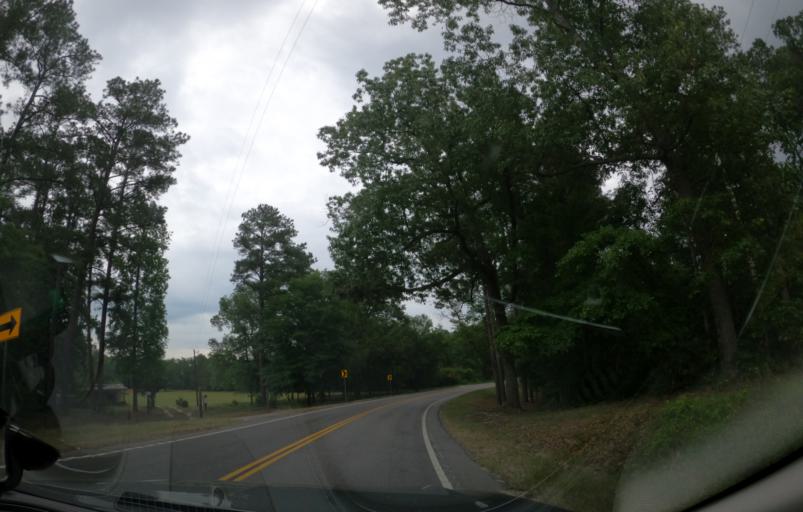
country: US
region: South Carolina
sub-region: Aiken County
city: Aiken
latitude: 33.5767
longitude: -81.6310
